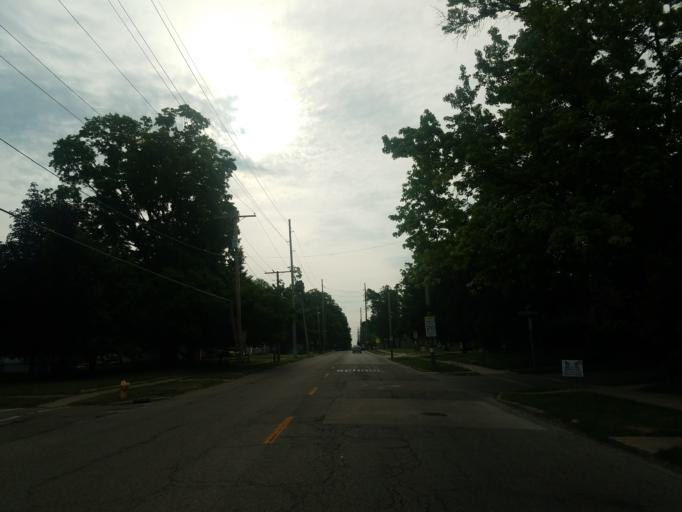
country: US
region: Illinois
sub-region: McLean County
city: Bloomington
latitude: 40.4740
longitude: -88.9710
